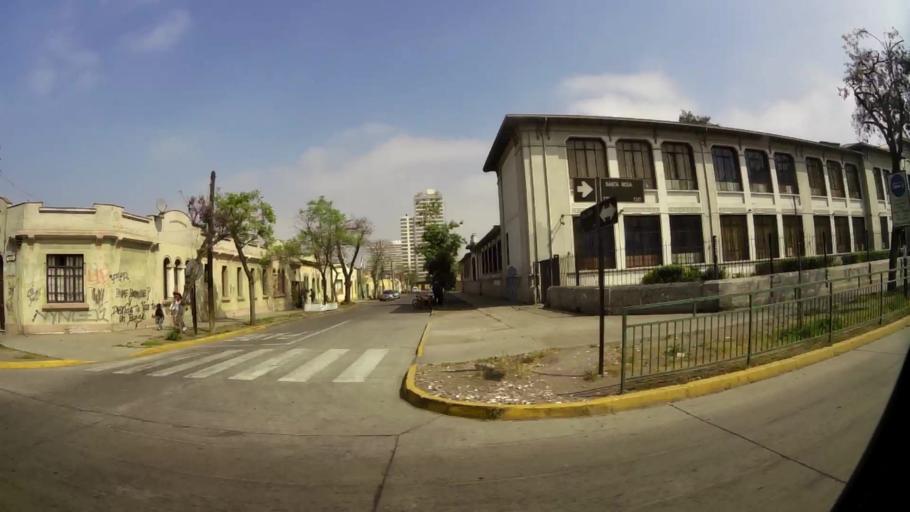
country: CL
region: Santiago Metropolitan
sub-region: Provincia de Santiago
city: Santiago
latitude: -33.4620
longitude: -70.6430
